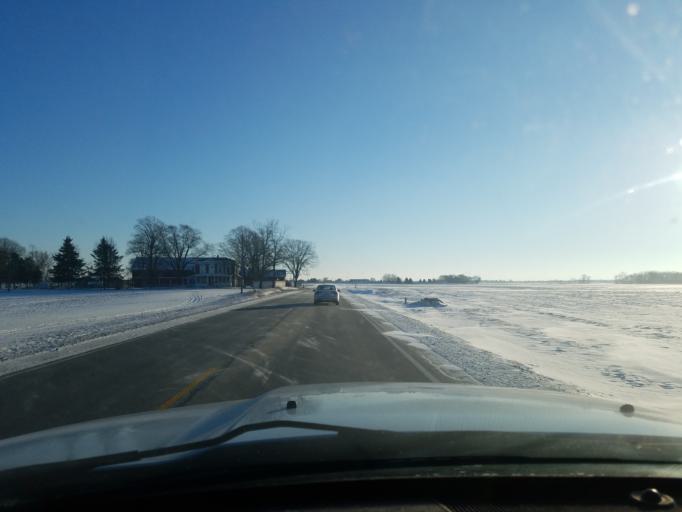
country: US
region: Indiana
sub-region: Noble County
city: Ligonier
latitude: 41.4518
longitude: -85.6168
